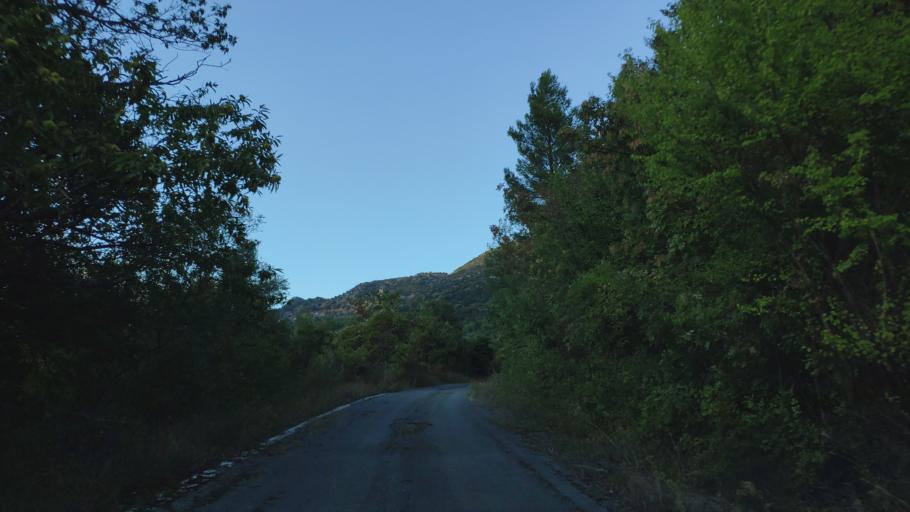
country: GR
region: Peloponnese
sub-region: Nomos Arkadias
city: Dimitsana
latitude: 37.5717
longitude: 22.0467
